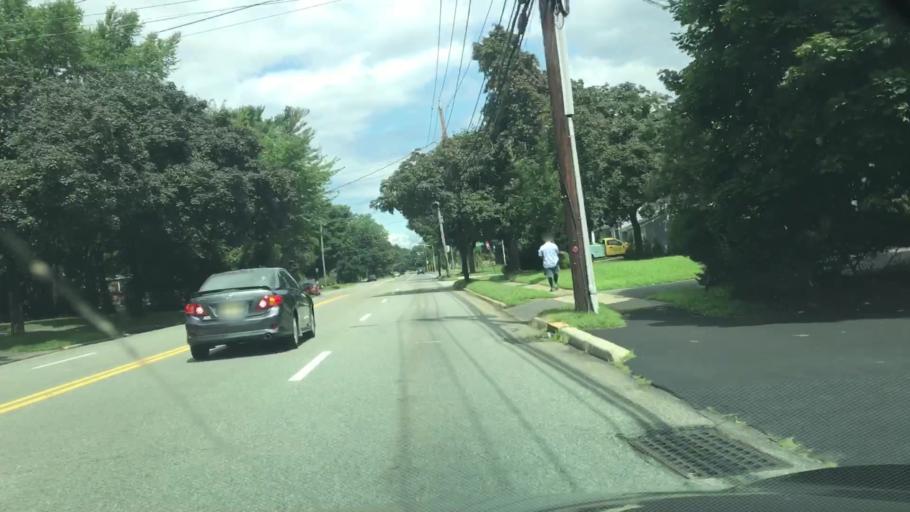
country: US
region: New Jersey
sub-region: Bergen County
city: River Edge
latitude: 40.9413
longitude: -74.0512
